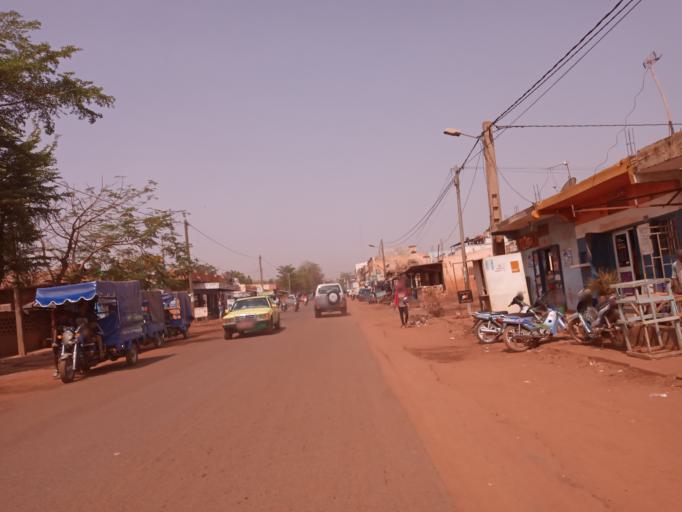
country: ML
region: Bamako
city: Bamako
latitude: 12.5888
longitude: -7.9857
